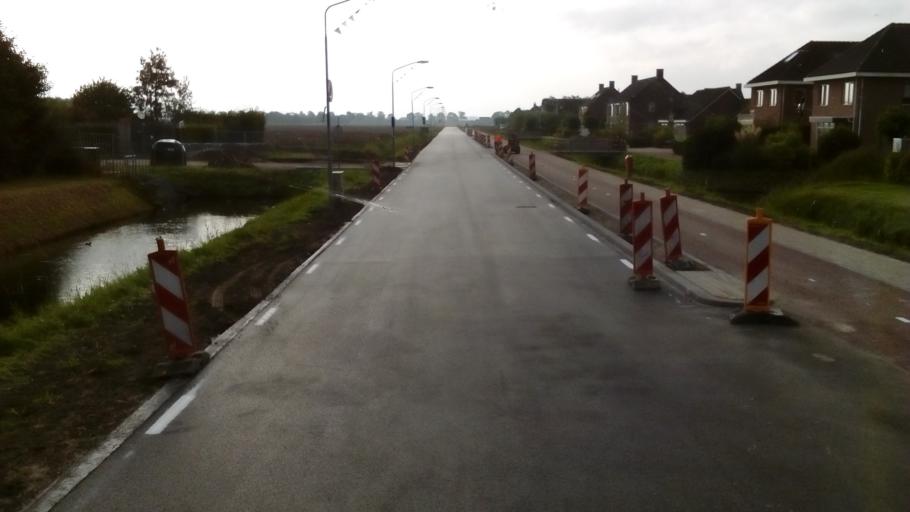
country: NL
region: North Brabant
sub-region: Gemeente Made en Drimmelen
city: Made
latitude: 51.6731
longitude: 4.6803
